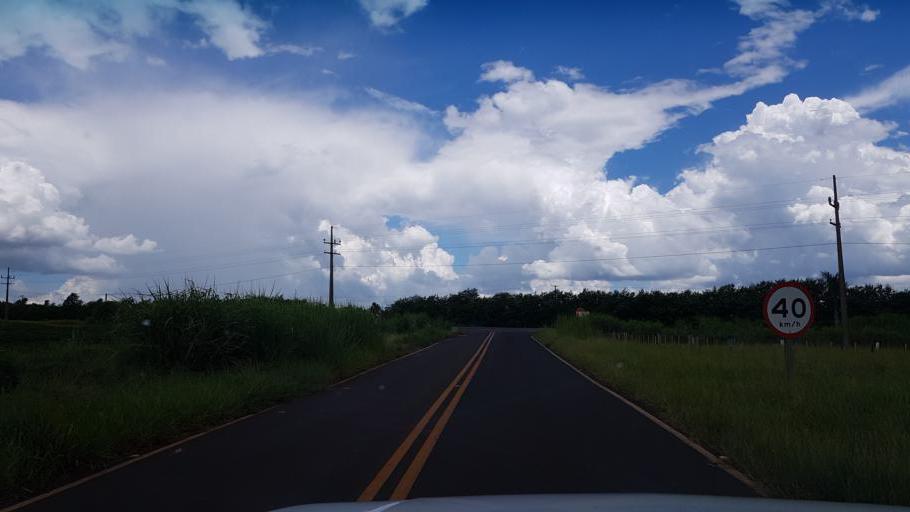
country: BR
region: Sao Paulo
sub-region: Paraguacu Paulista
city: Paraguacu Paulista
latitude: -22.3647
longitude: -50.6291
